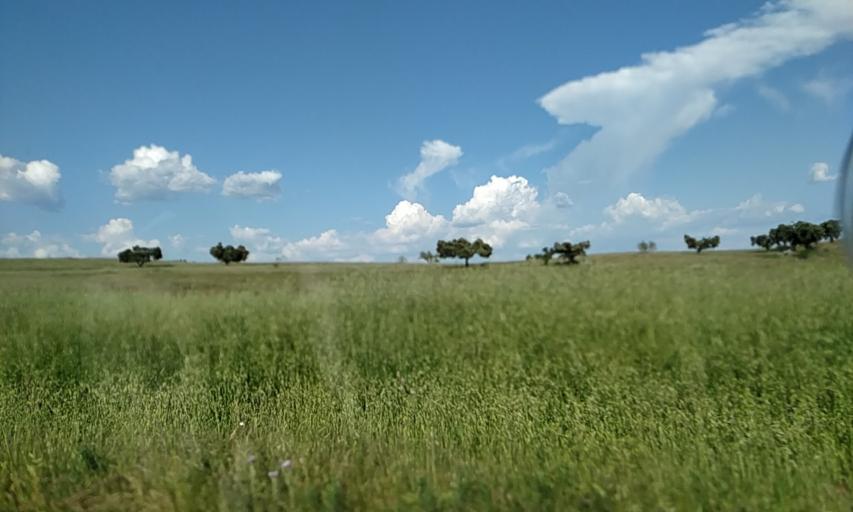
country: PT
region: Portalegre
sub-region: Portalegre
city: Urra
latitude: 39.0910
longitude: -7.4375
